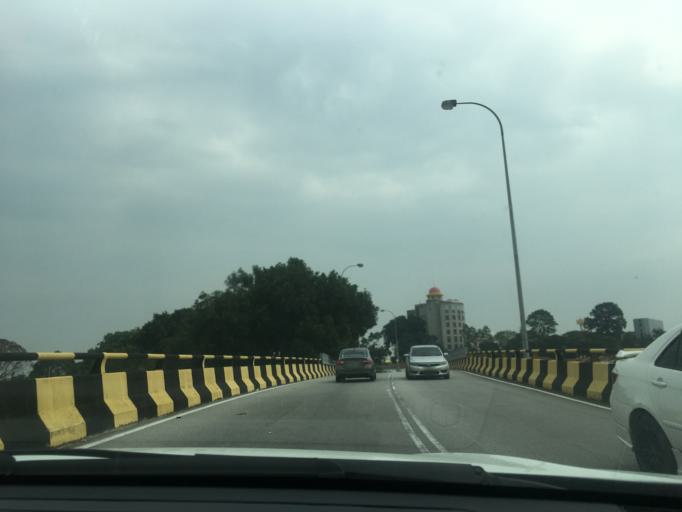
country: MY
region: Selangor
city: Klang
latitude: 3.0470
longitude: 101.4424
